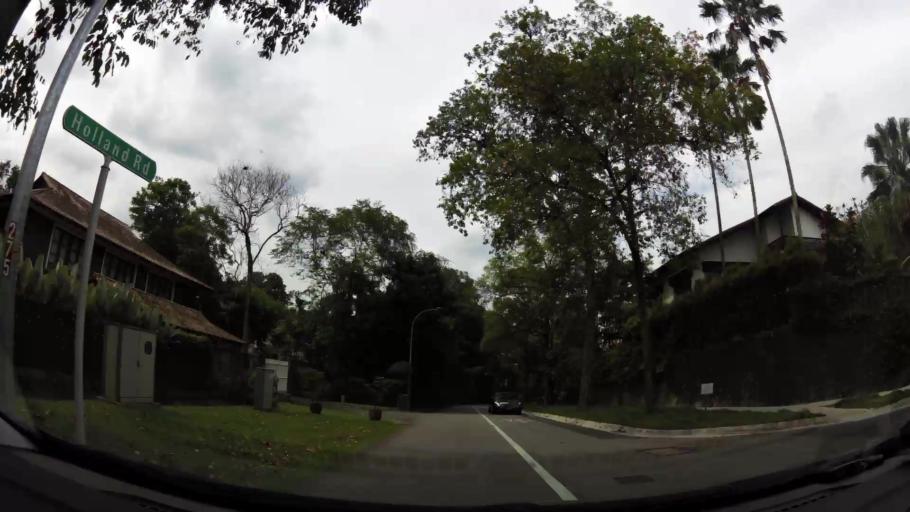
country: SG
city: Singapore
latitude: 1.3240
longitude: 103.7854
